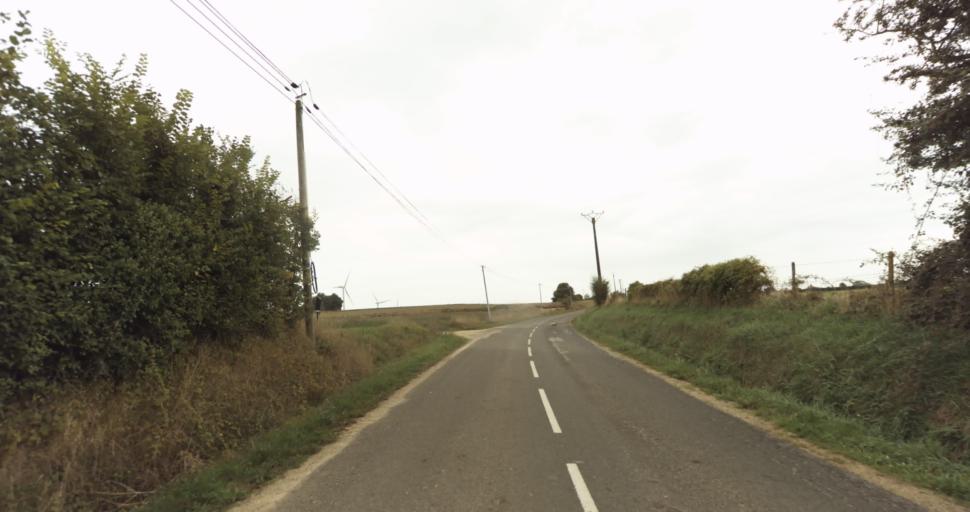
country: FR
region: Lower Normandy
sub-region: Departement de l'Orne
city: Sainte-Gauburge-Sainte-Colombe
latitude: 48.7302
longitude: 0.3608
